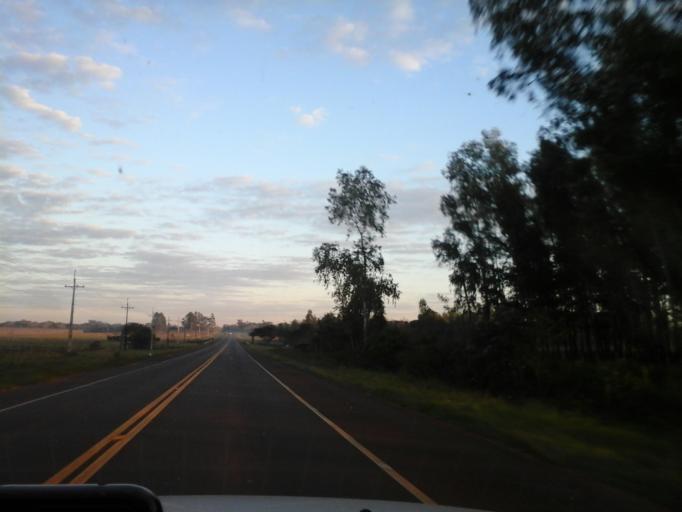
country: PY
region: Misiones
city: Santiago
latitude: -27.0418
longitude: -56.6609
